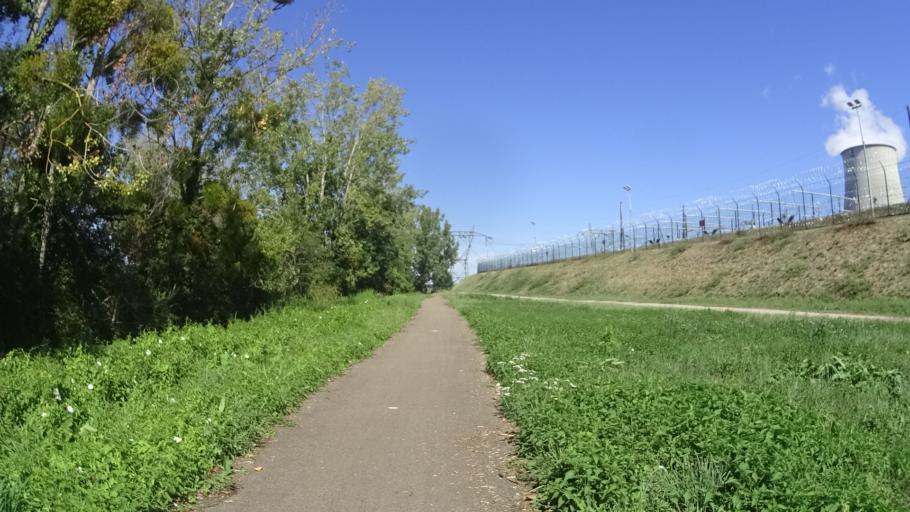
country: FR
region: Centre
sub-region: Departement du Cher
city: Belleville-sur-Loire
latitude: 47.5054
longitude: 2.8688
